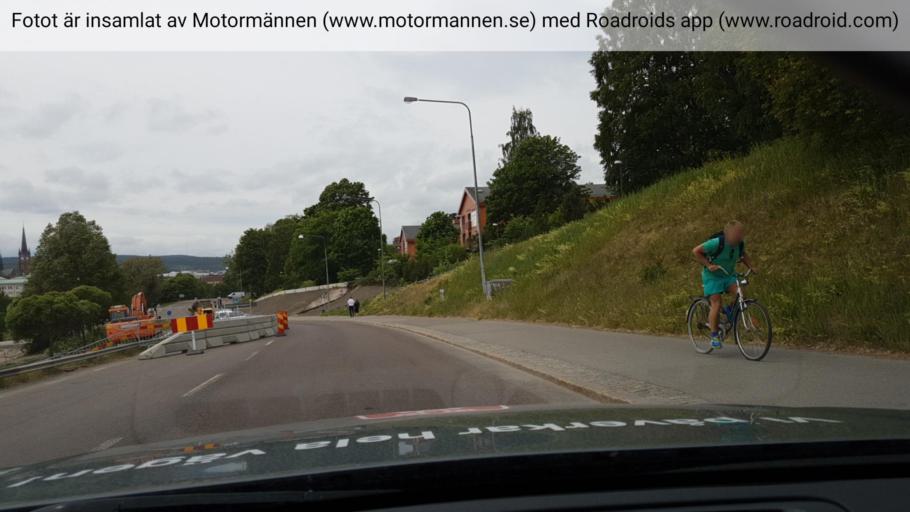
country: SE
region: Vaesternorrland
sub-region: Sundsvalls Kommun
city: Sundsvall
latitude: 62.3952
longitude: 17.3156
